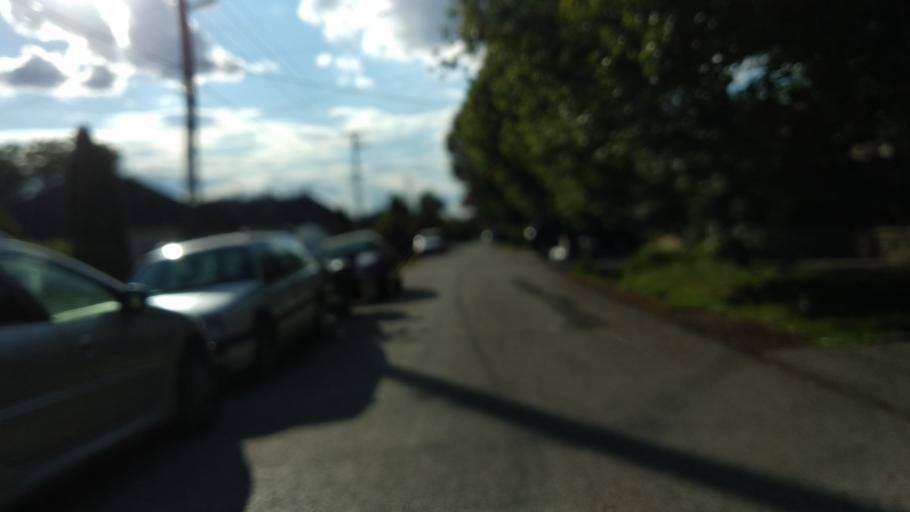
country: HU
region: Pest
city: Godollo
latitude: 47.5881
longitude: 19.3497
